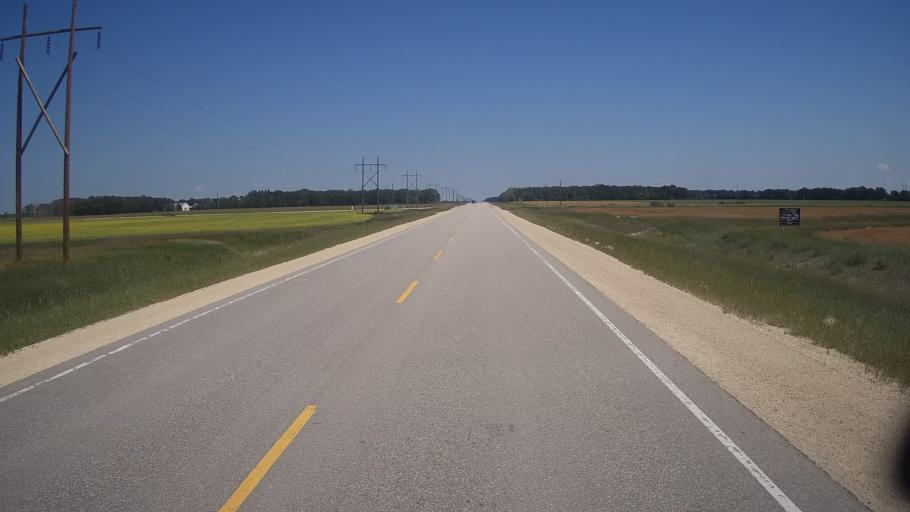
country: CA
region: Manitoba
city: Stonewall
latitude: 50.1227
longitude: -97.4863
